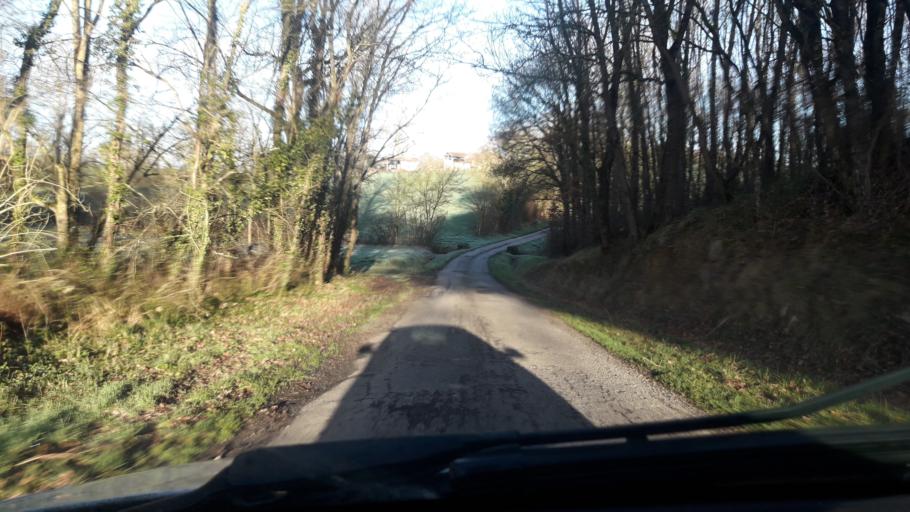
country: FR
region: Midi-Pyrenees
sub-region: Departement du Gers
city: Gimont
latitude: 43.6473
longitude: 0.9700
